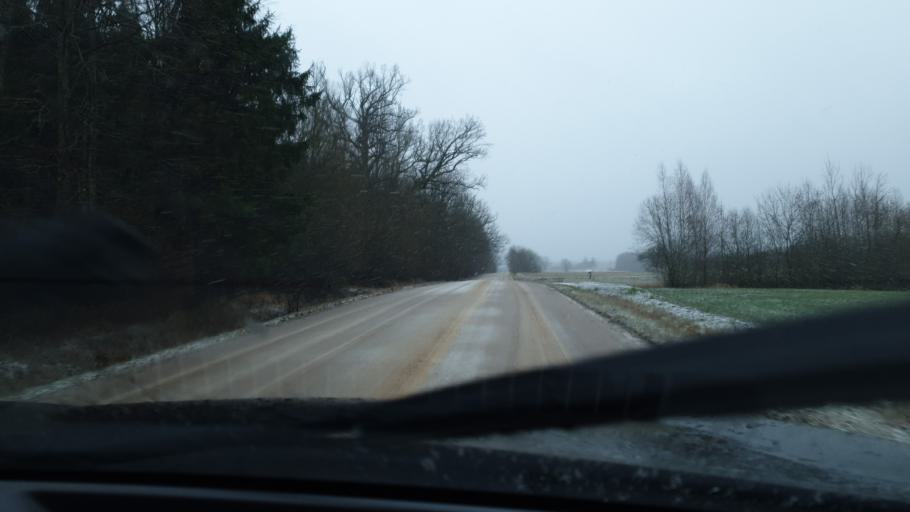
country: LT
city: Jieznas
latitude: 54.5654
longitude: 24.3179
